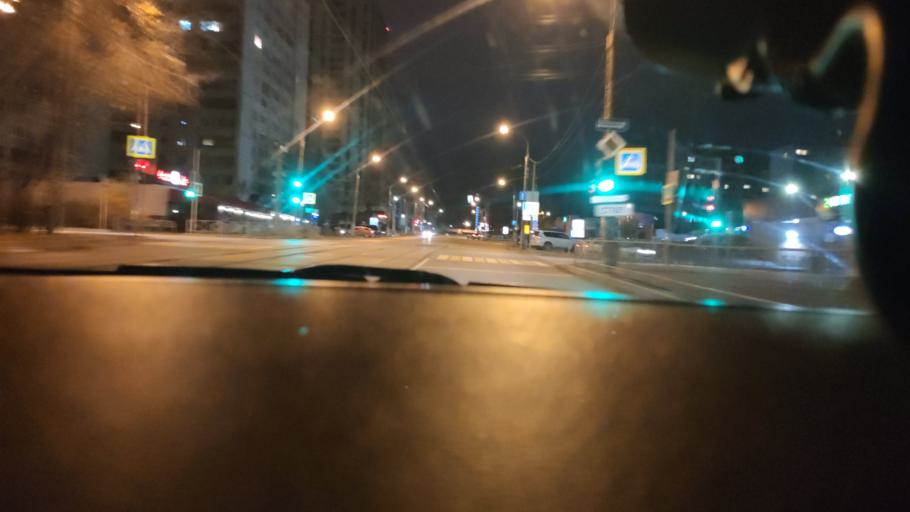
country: RU
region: Perm
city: Perm
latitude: 58.0059
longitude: 56.2212
